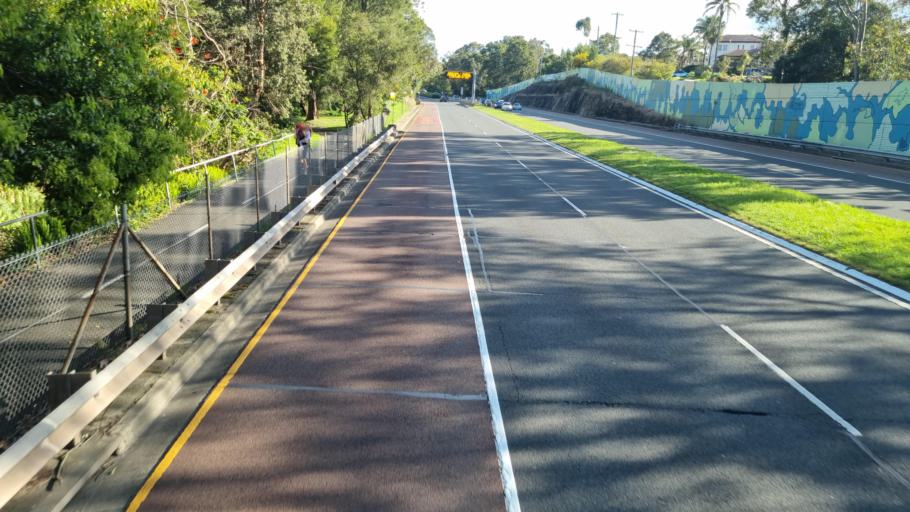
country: AU
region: New South Wales
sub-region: Manly Vale
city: Balgowlah
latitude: -33.7905
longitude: 151.2557
